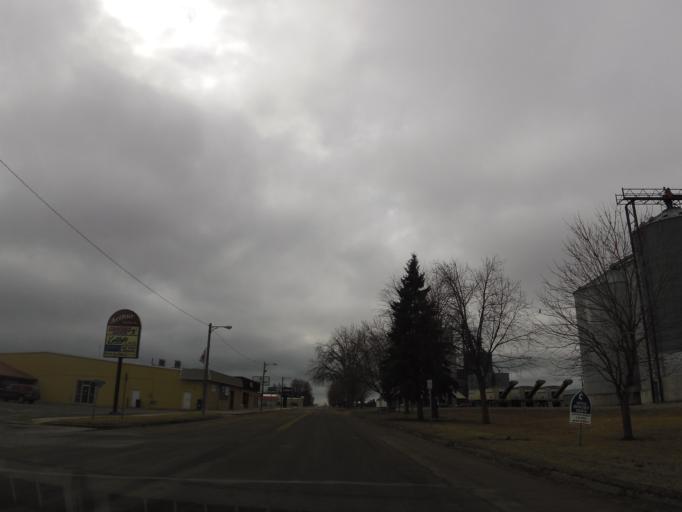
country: US
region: North Dakota
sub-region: Cass County
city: Casselton
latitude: 47.1044
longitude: -97.2182
